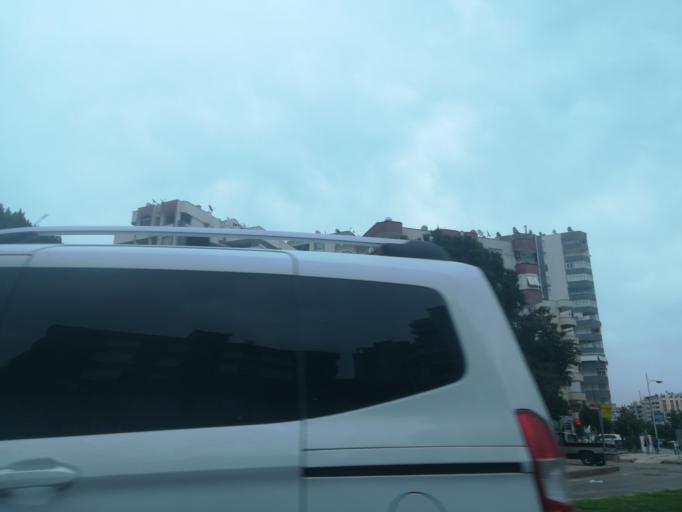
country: TR
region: Adana
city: Adana
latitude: 37.0325
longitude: 35.3093
